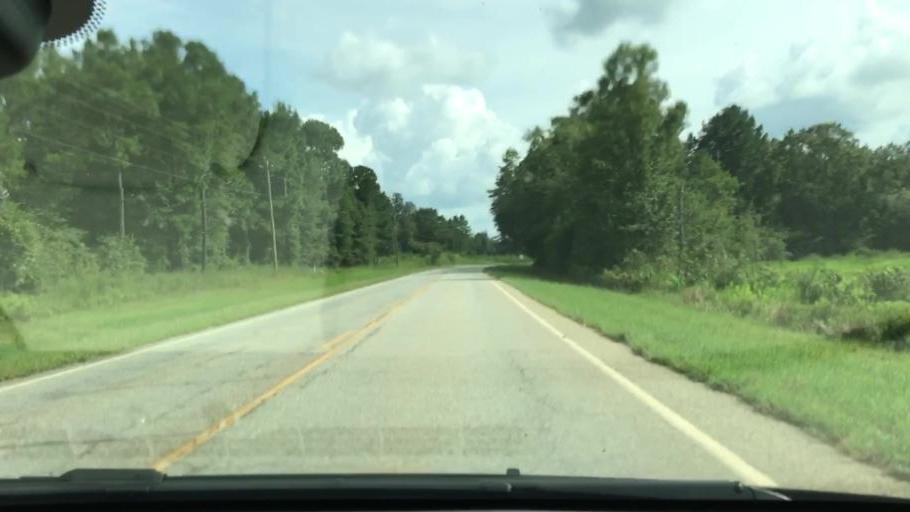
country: US
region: Georgia
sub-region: Clay County
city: Fort Gaines
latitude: 31.7144
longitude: -85.0419
